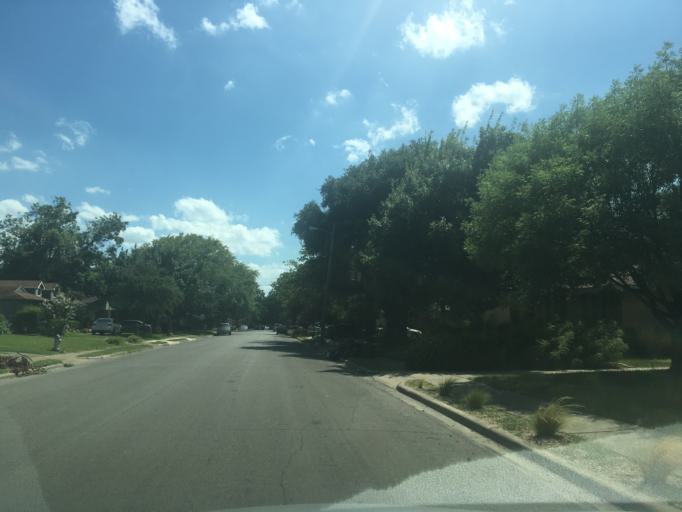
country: US
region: Texas
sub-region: Dallas County
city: Garland
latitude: 32.8322
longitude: -96.6777
